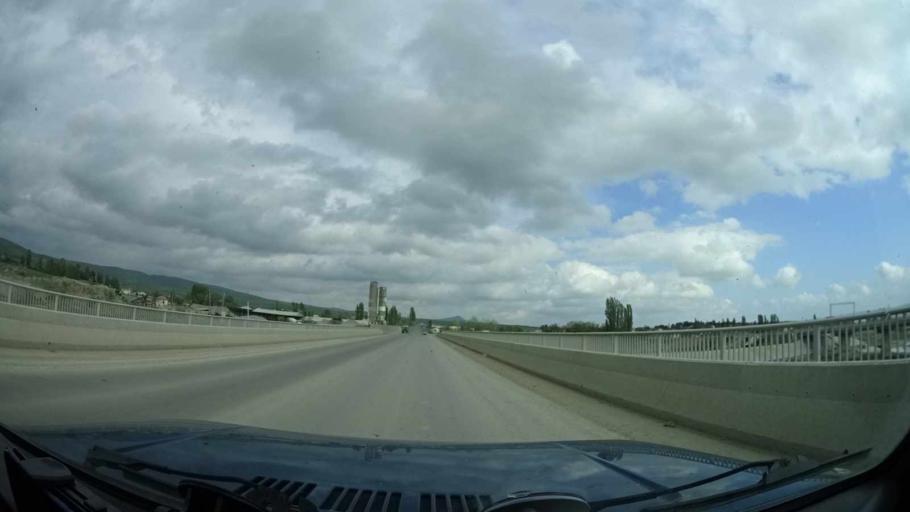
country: AZ
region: Samaxi
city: Shamakhi
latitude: 40.5956
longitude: 48.6992
